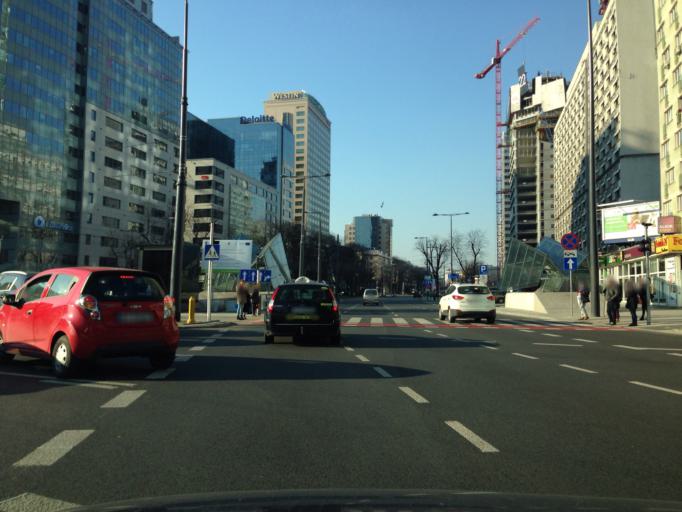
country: PL
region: Masovian Voivodeship
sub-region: Warszawa
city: Wola
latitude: 52.2333
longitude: 20.9987
